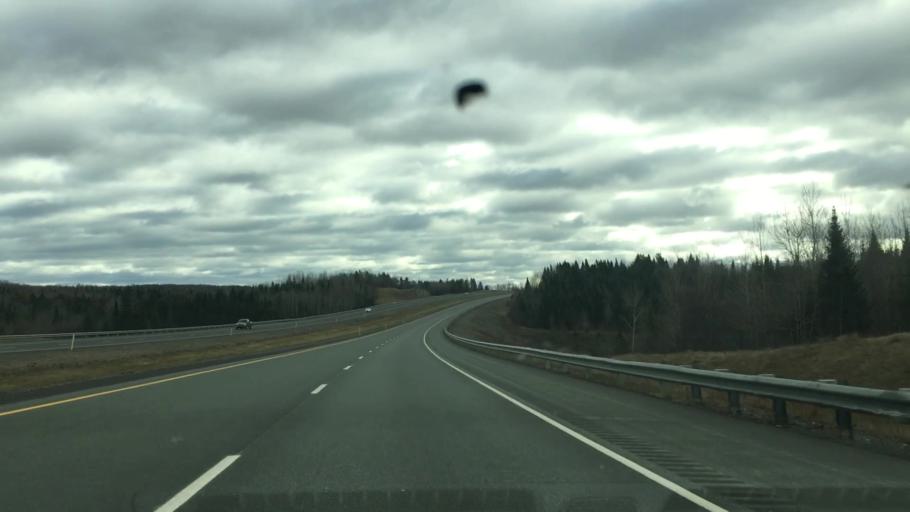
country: CA
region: New Brunswick
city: Florenceville-Bristol
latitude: 46.5417
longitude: -67.7148
